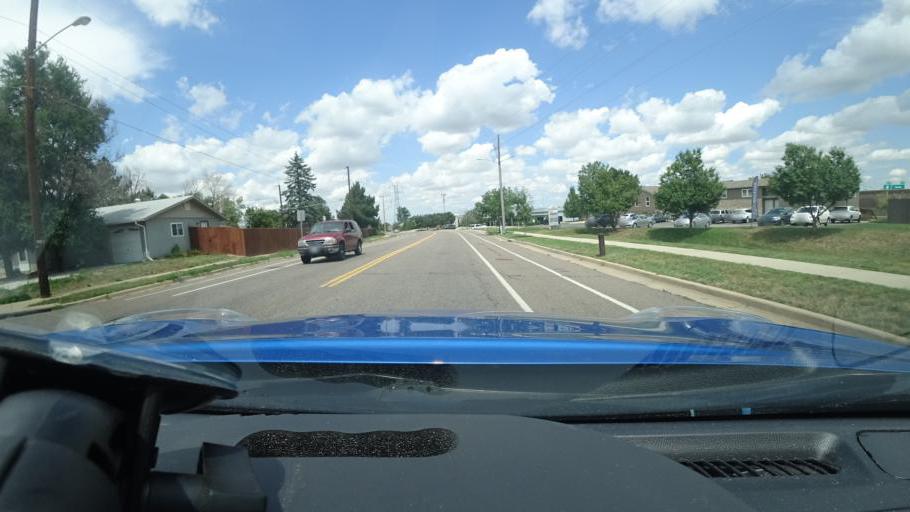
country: US
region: Colorado
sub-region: Adams County
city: Aurora
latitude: 39.7074
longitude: -104.8287
